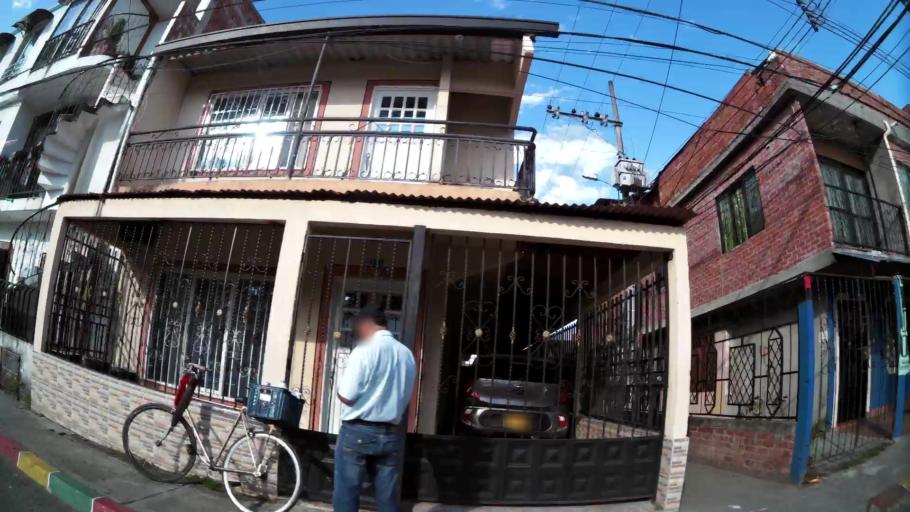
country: CO
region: Valle del Cauca
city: Cali
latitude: 3.4014
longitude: -76.5067
